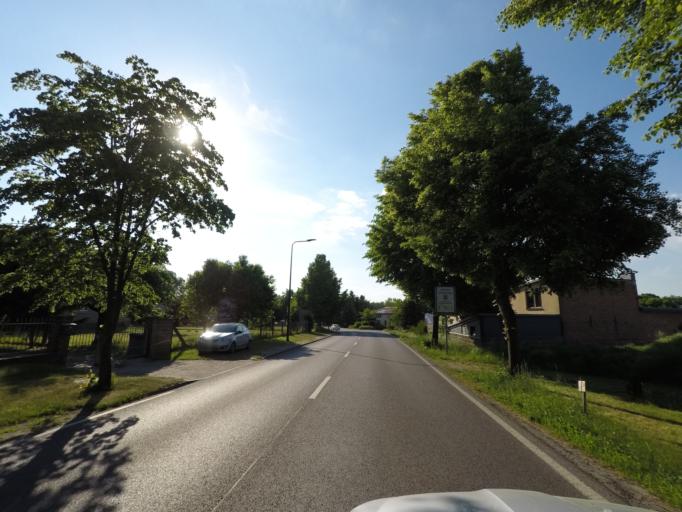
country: DE
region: Brandenburg
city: Hohenfinow
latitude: 52.8184
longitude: 13.8967
